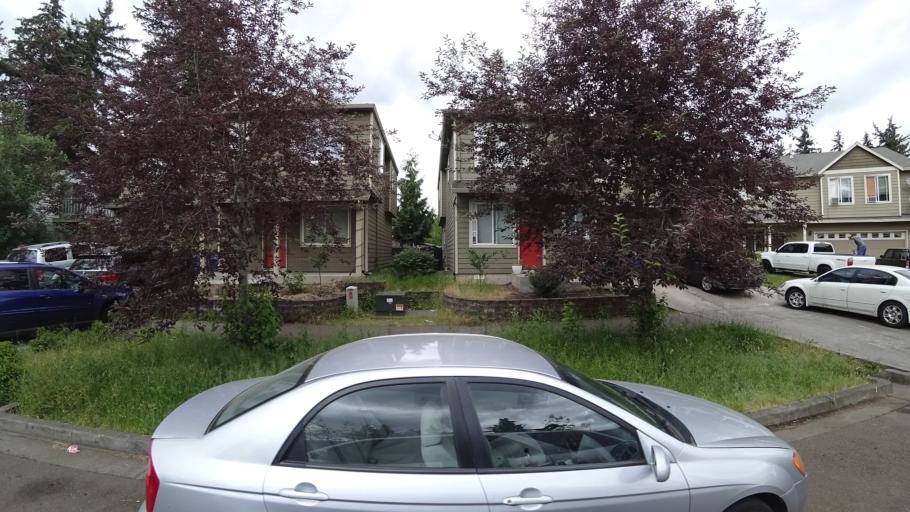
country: US
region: Oregon
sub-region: Multnomah County
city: Lents
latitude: 45.4949
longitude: -122.5325
